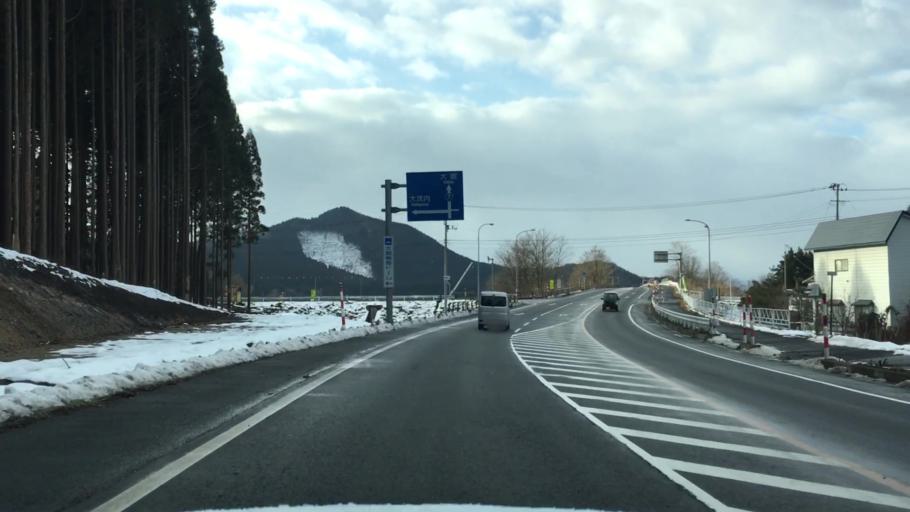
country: JP
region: Akita
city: Odate
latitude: 40.3483
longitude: 140.6005
